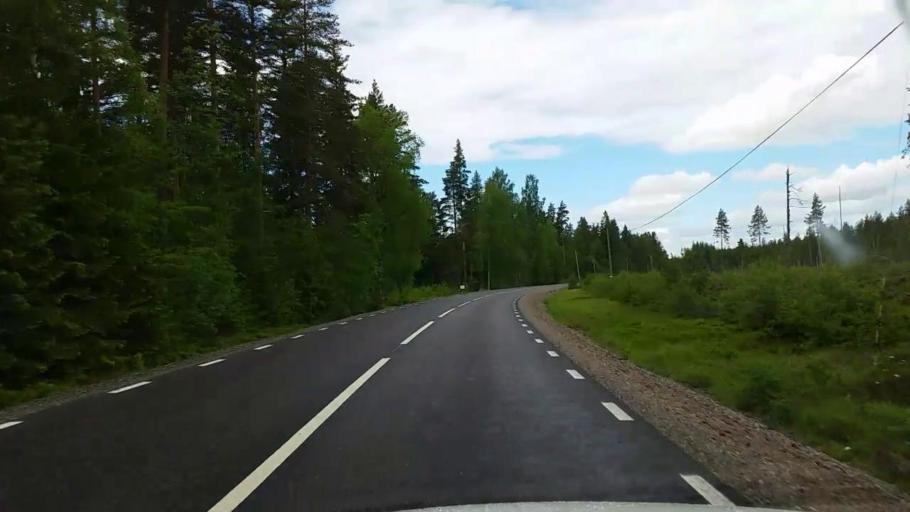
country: SE
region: Gaevleborg
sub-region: Sandvikens Kommun
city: Jarbo
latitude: 60.8522
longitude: 16.4454
